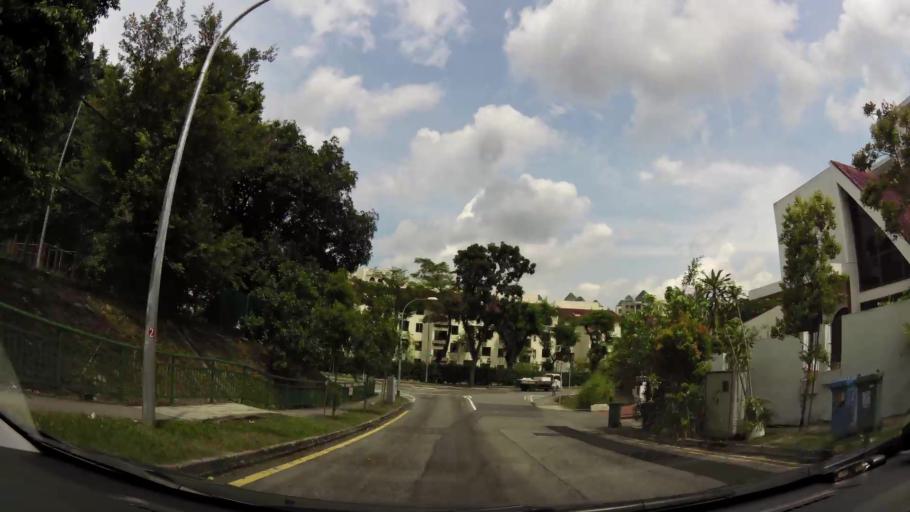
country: SG
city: Singapore
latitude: 1.3392
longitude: 103.7686
